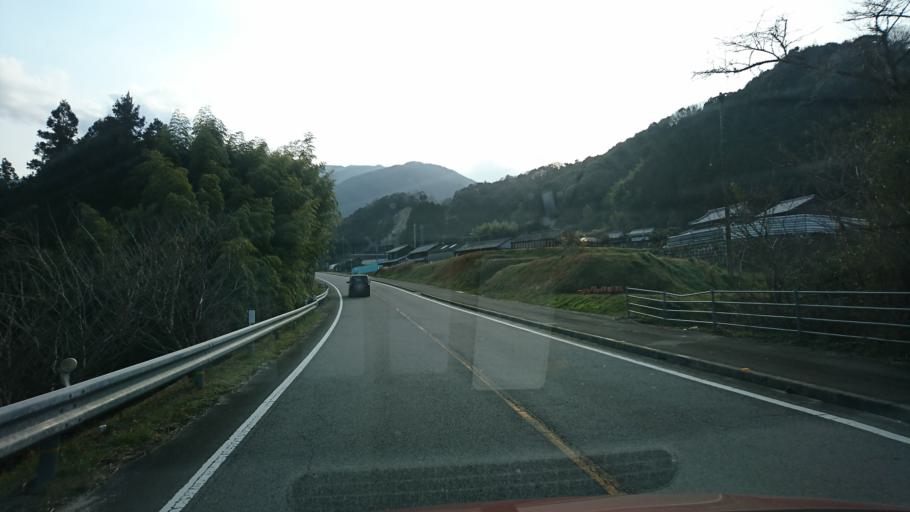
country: JP
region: Ehime
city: Hojo
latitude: 33.9774
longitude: 132.9046
